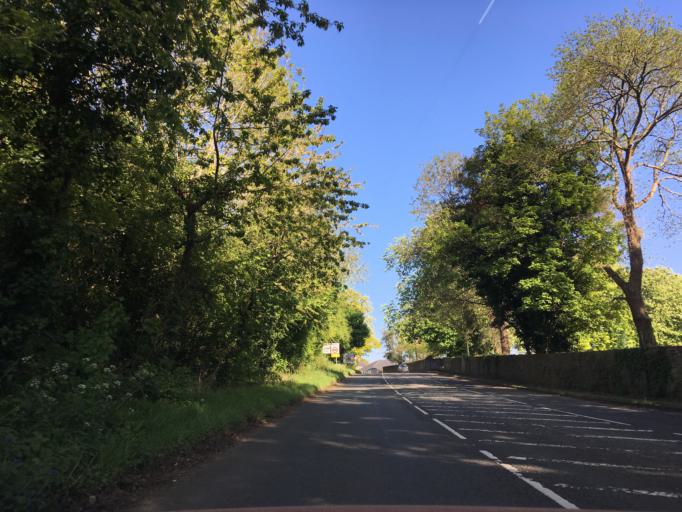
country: GB
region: Wales
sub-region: Monmouthshire
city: Chepstow
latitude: 51.6492
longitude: -2.6714
